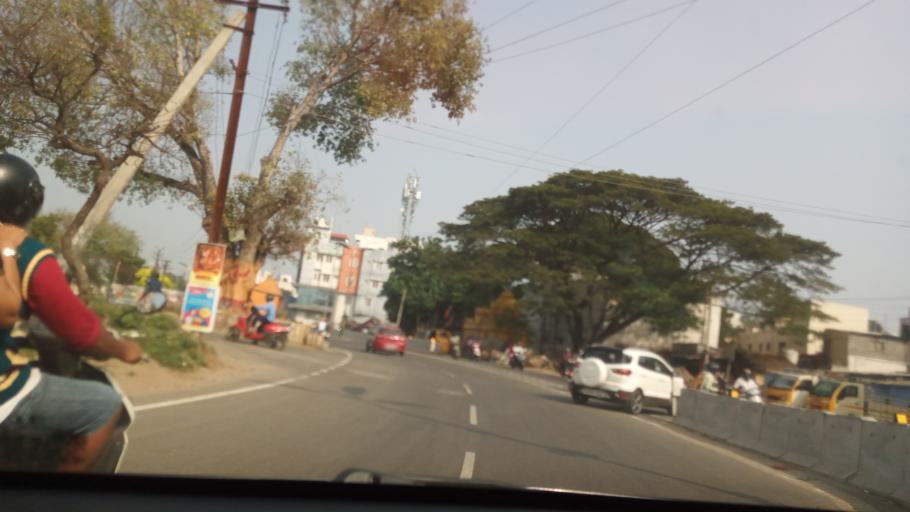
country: IN
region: Tamil Nadu
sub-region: Coimbatore
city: Coimbatore
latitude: 11.0025
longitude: 76.9483
